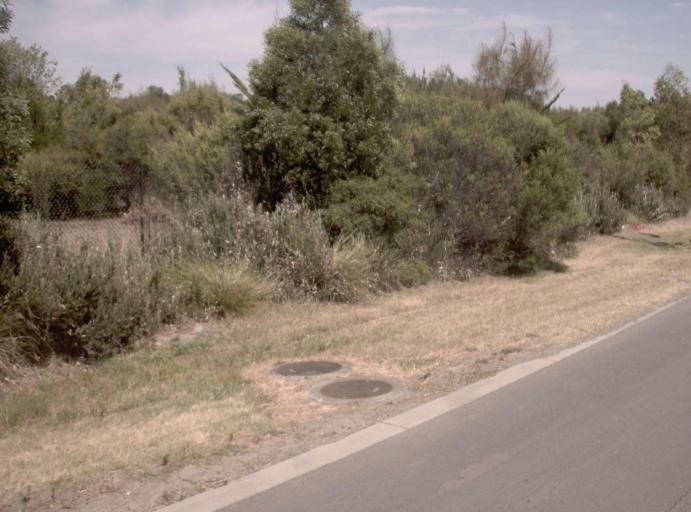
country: AU
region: Victoria
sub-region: Casey
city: Eumemmerring
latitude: -37.9947
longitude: 145.2636
